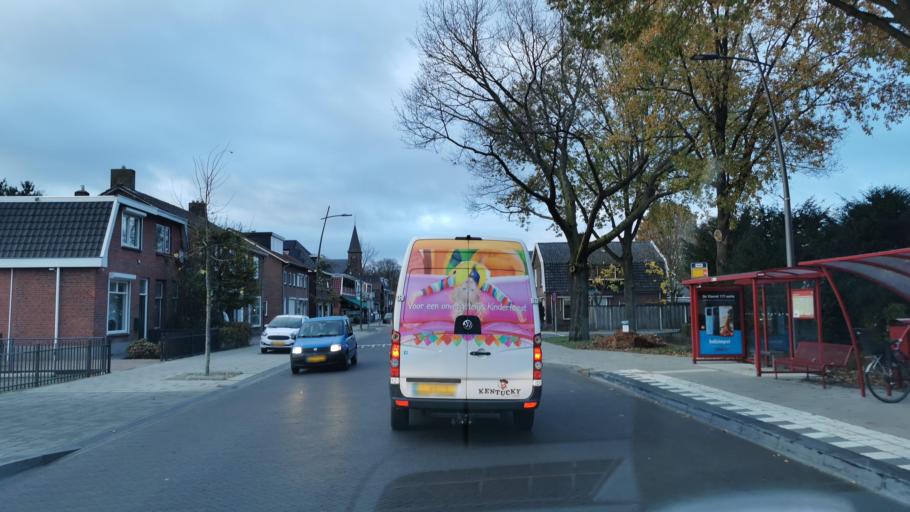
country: DE
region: North Rhine-Westphalia
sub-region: Regierungsbezirk Munster
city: Gronau
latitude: 52.2387
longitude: 7.0339
